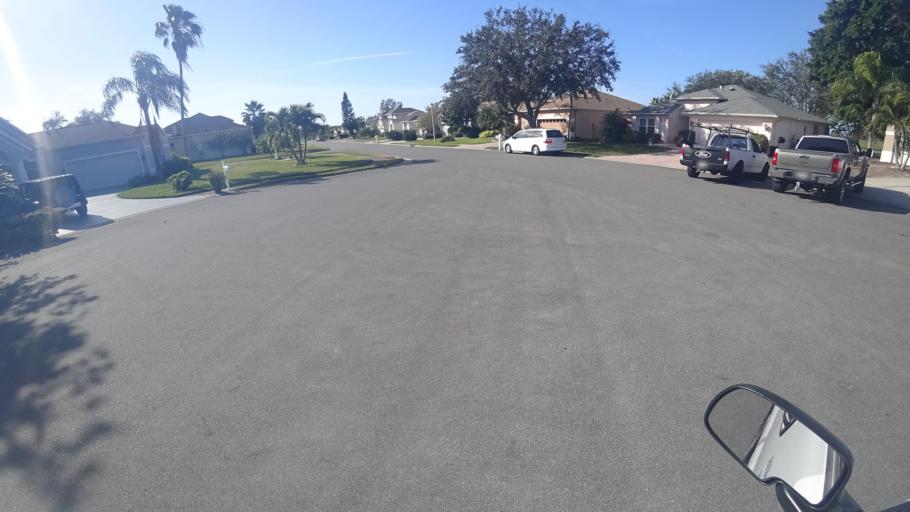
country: US
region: Florida
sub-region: Manatee County
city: South Bradenton
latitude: 27.4519
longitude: -82.6152
